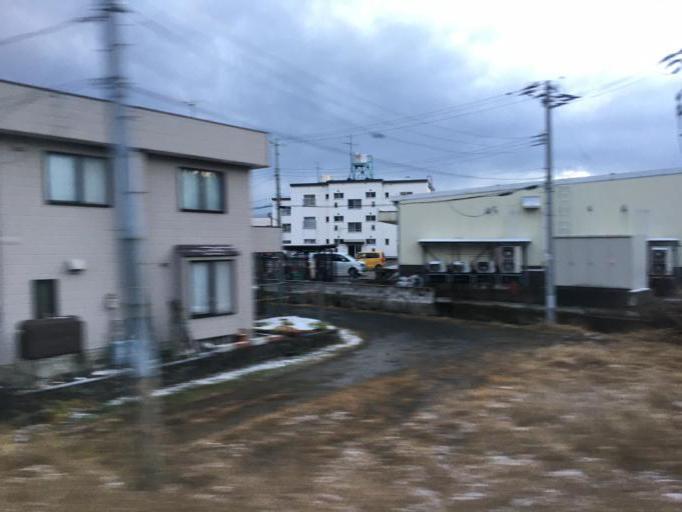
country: JP
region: Aomori
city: Aomori Shi
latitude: 40.8286
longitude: 140.6768
